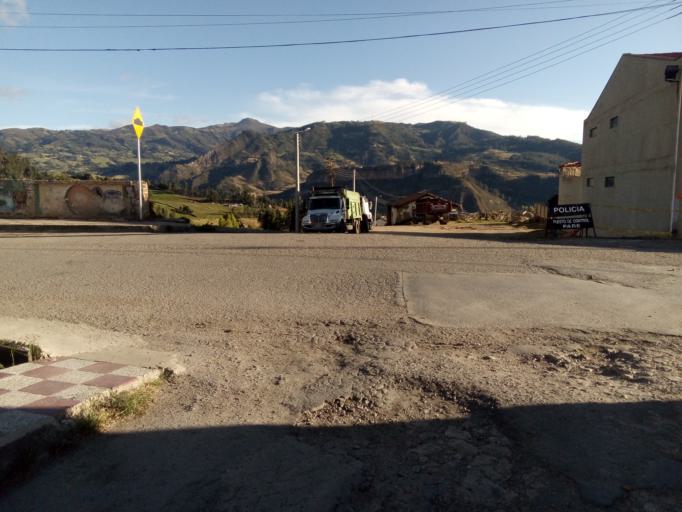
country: CO
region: Boyaca
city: Gameza
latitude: 5.8018
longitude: -72.8059
